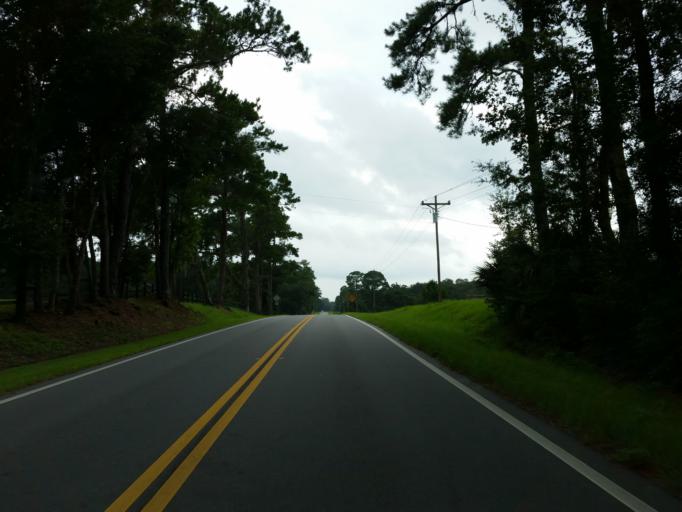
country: US
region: Florida
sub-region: Levy County
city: Williston
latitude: 29.3982
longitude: -82.3893
